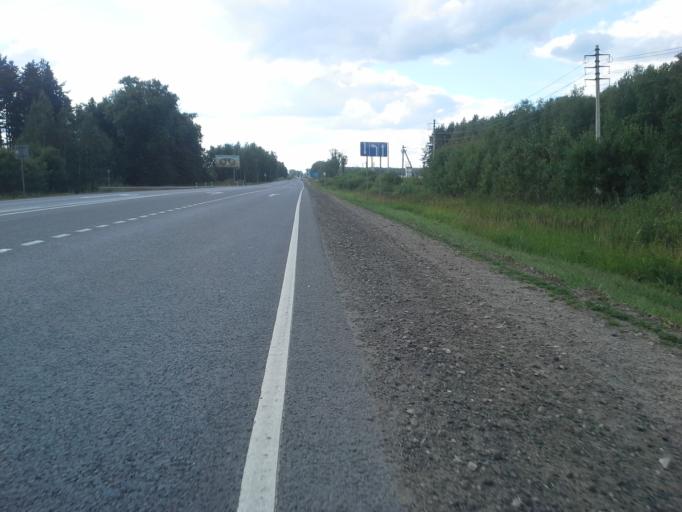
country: RU
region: Moskovskaya
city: L'vovskiy
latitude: 55.3390
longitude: 37.4657
